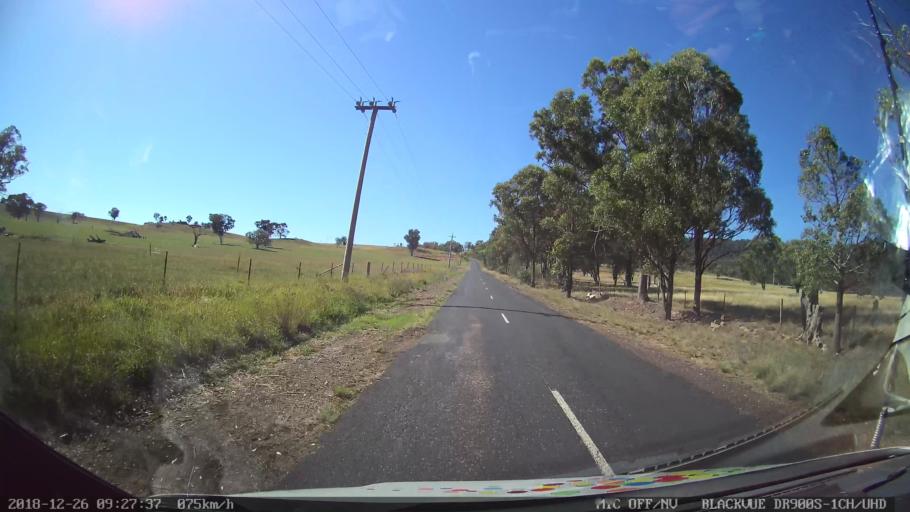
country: AU
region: New South Wales
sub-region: Mid-Western Regional
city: Kandos
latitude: -32.8376
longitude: 150.0179
